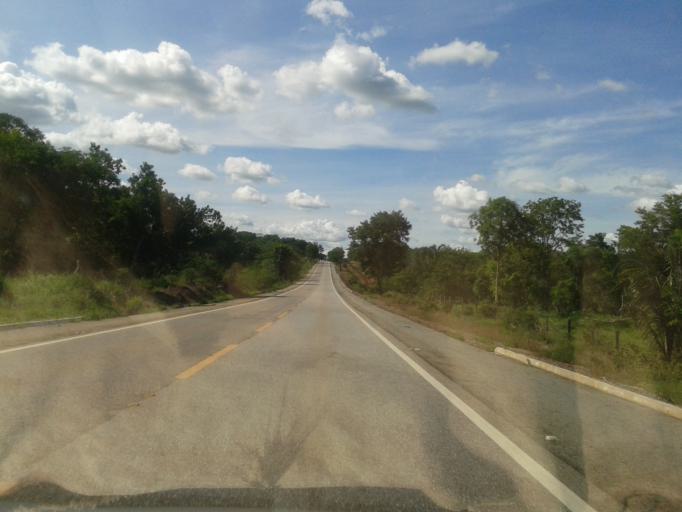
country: BR
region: Goias
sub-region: Mozarlandia
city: Mozarlandia
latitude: -15.2007
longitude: -50.5431
